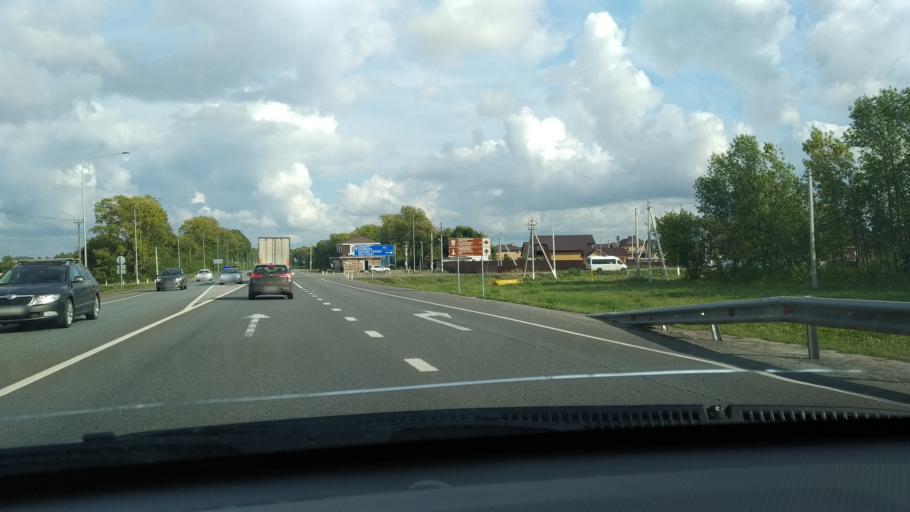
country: RU
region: Tatarstan
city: Stolbishchi
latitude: 55.6564
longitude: 49.3104
